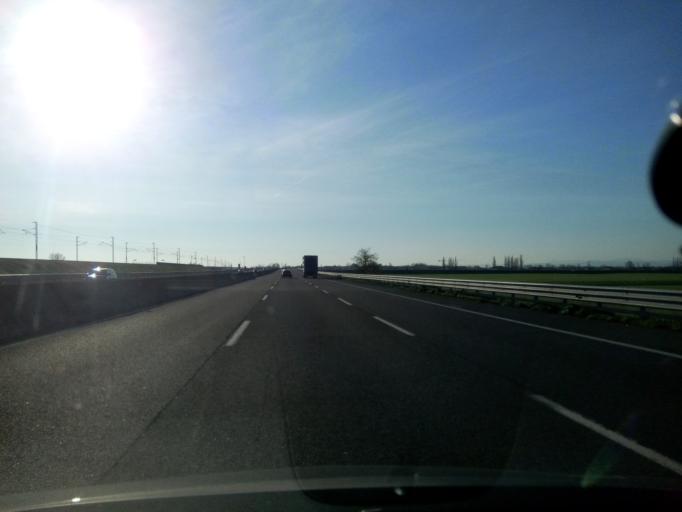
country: IT
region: Emilia-Romagna
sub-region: Provincia di Reggio Emilia
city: Roncocesi
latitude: 44.7478
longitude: 10.5623
